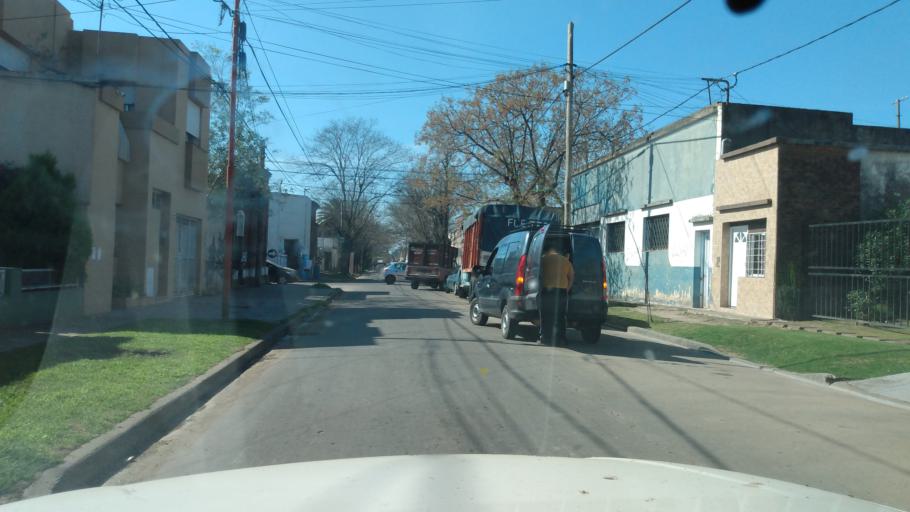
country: AR
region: Buenos Aires
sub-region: Partido de Lujan
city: Lujan
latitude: -34.5718
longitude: -59.1005
